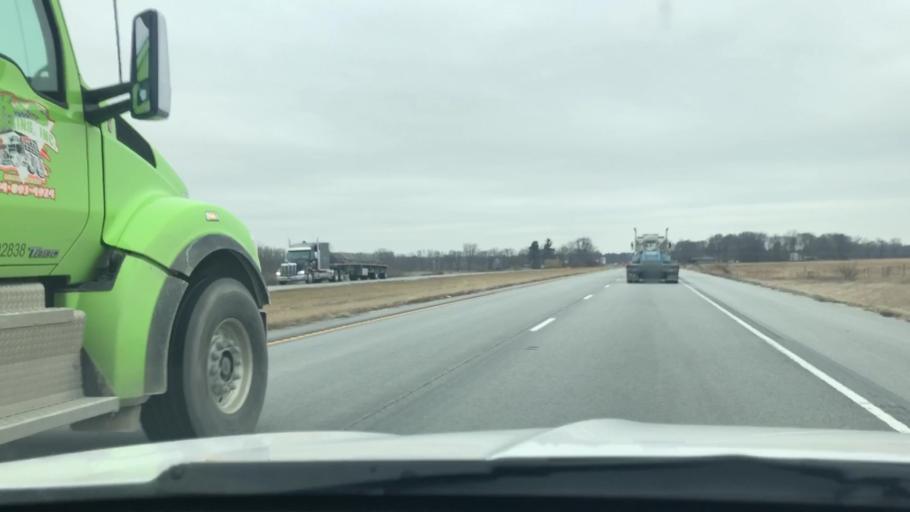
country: US
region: Indiana
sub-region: Miami County
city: Peru
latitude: 40.8105
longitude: -86.1290
